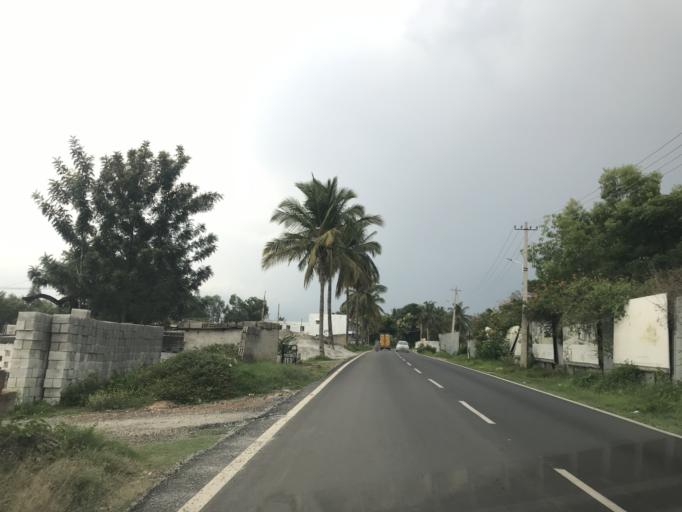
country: IN
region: Karnataka
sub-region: Bangalore Rural
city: Devanhalli
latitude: 13.1784
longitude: 77.6493
